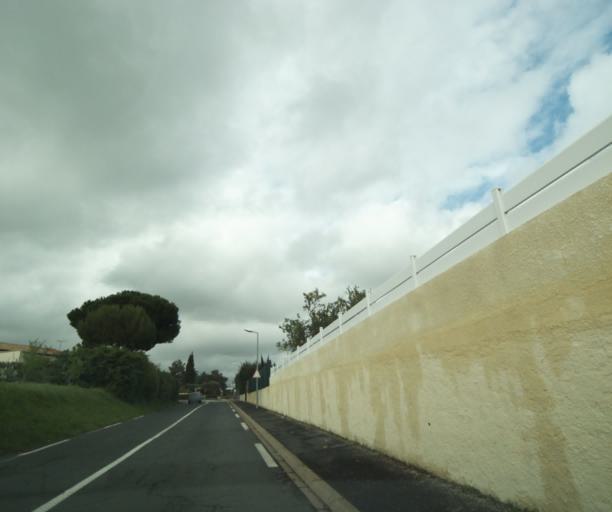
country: FR
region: Languedoc-Roussillon
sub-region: Departement de l'Herault
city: Pignan
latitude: 43.5878
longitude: 3.7671
